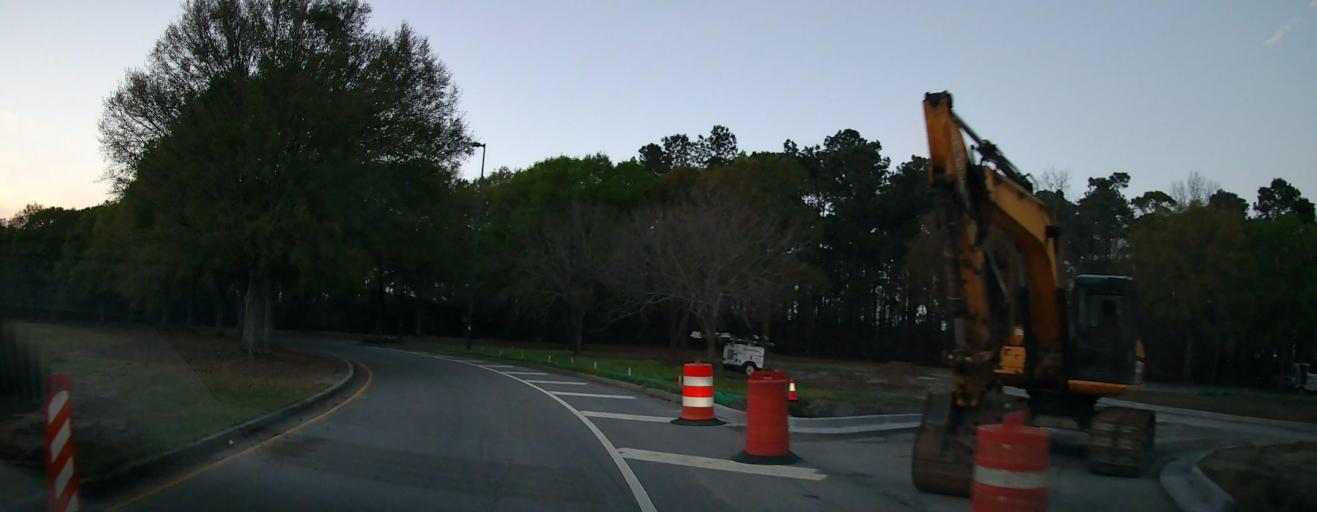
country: US
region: Georgia
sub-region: Chatham County
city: Pooler
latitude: 32.1377
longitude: -81.2104
